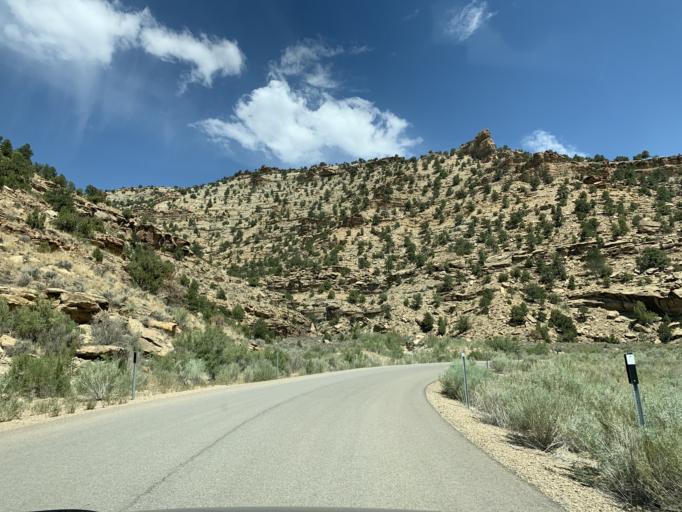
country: US
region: Utah
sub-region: Carbon County
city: East Carbon City
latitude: 39.8178
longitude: -110.2542
